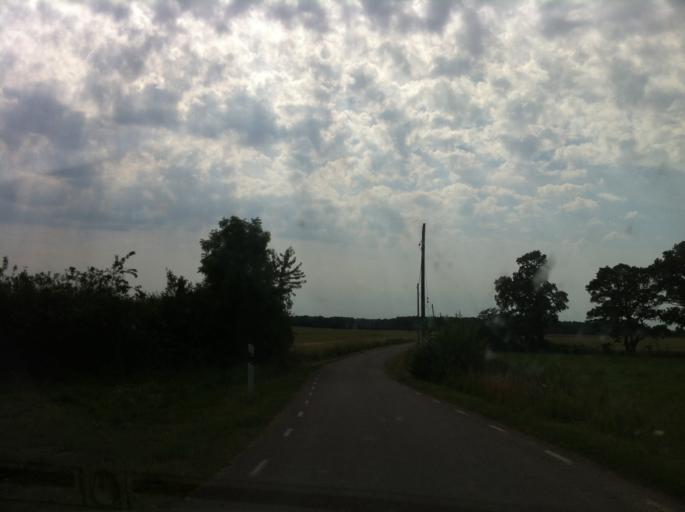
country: SE
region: Skane
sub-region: Eslovs Kommun
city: Eslov
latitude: 55.9226
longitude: 13.2520
